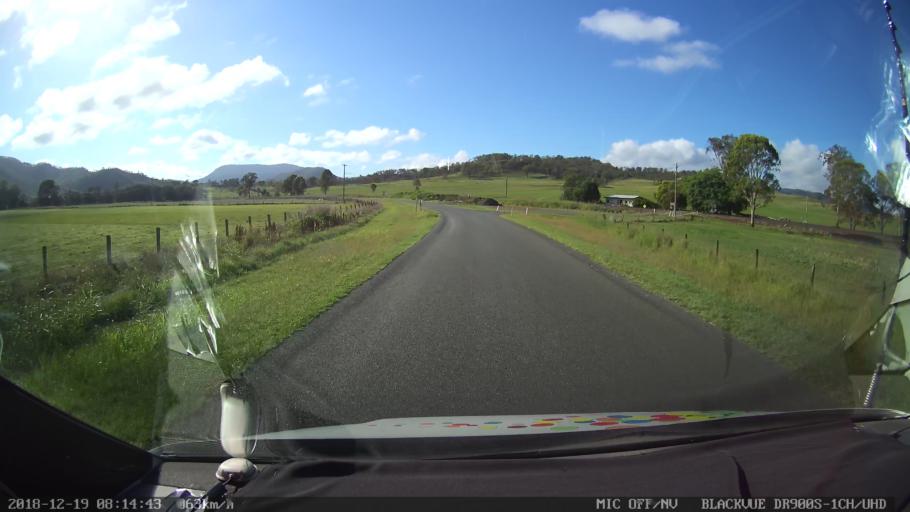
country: AU
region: Queensland
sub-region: Logan
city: Cedar Vale
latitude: -28.2499
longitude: 152.8919
